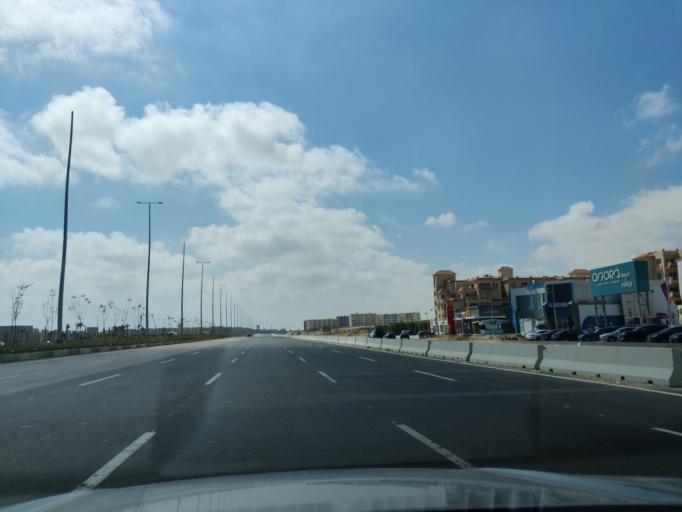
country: EG
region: Muhafazat Matruh
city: Al `Alamayn
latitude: 30.9607
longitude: 28.7578
